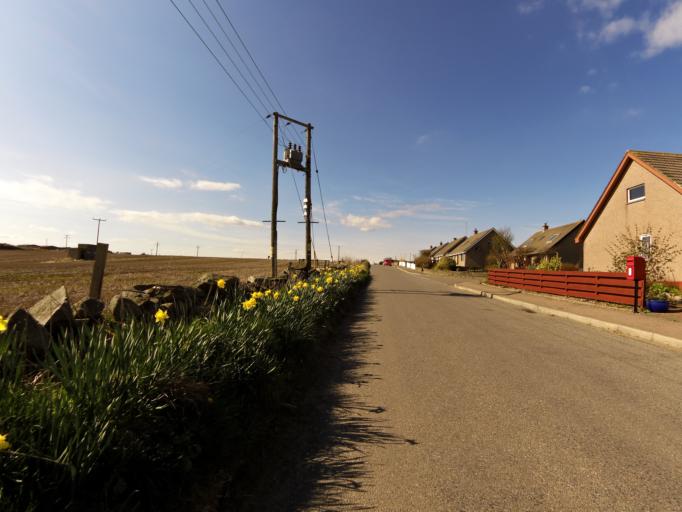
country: GB
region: Scotland
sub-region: Aberdeenshire
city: Portlethen
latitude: 57.0687
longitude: -2.1072
